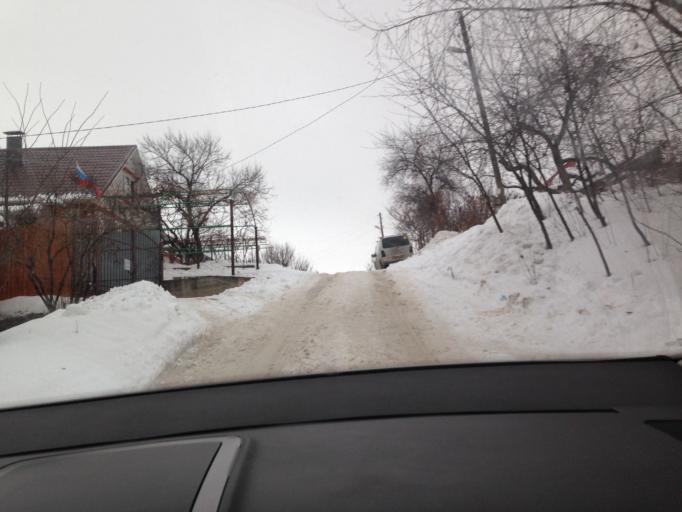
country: RU
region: Voronezj
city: Voronezh
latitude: 51.6400
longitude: 39.1937
